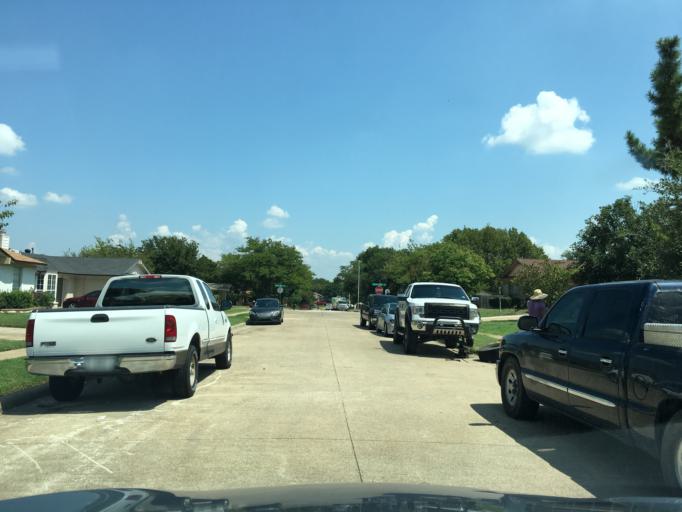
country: US
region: Texas
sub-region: Dallas County
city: Garland
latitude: 32.9427
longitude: -96.6542
